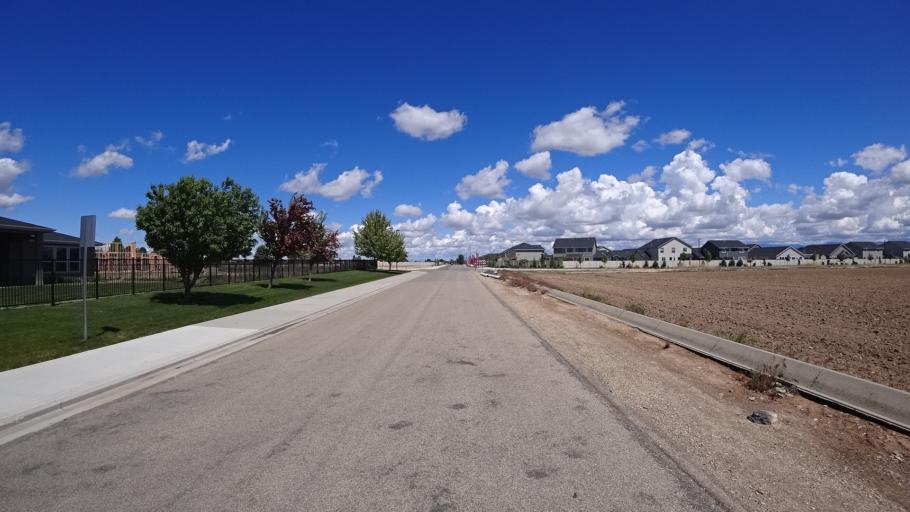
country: US
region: Idaho
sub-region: Ada County
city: Kuna
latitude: 43.5095
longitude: -116.4238
